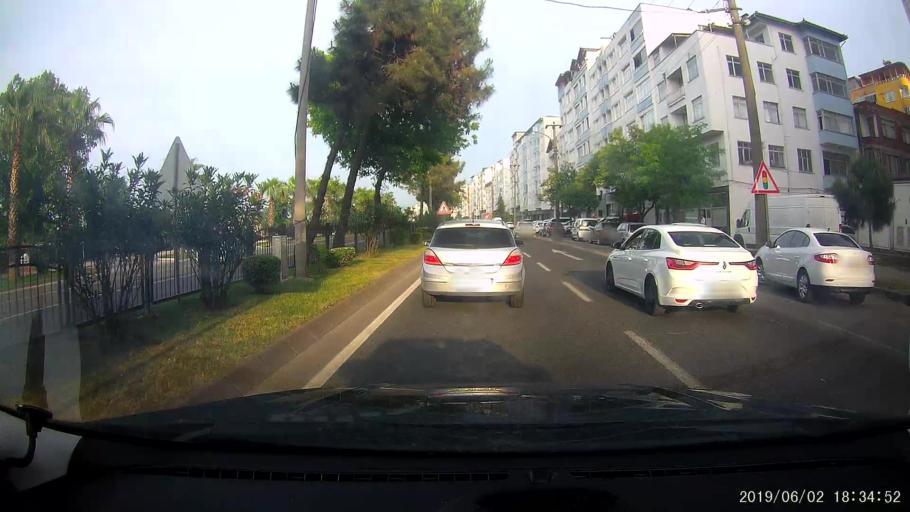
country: TR
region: Ordu
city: Fatsa
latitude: 41.0279
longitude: 37.5087
